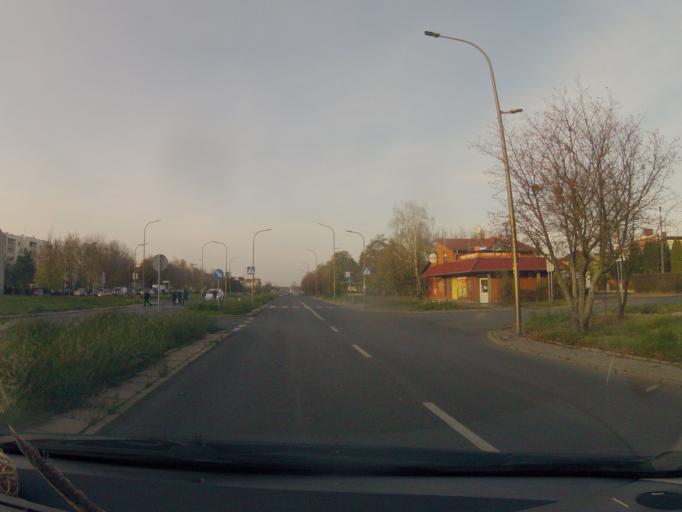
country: PL
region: Opole Voivodeship
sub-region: Powiat opolski
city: Opole
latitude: 50.6719
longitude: 17.9755
